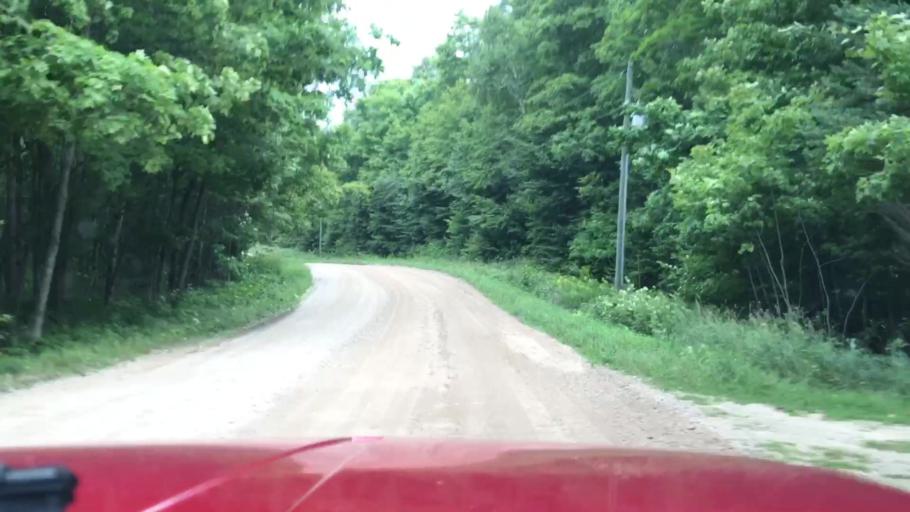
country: US
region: Michigan
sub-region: Charlevoix County
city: Charlevoix
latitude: 45.7354
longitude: -85.5580
